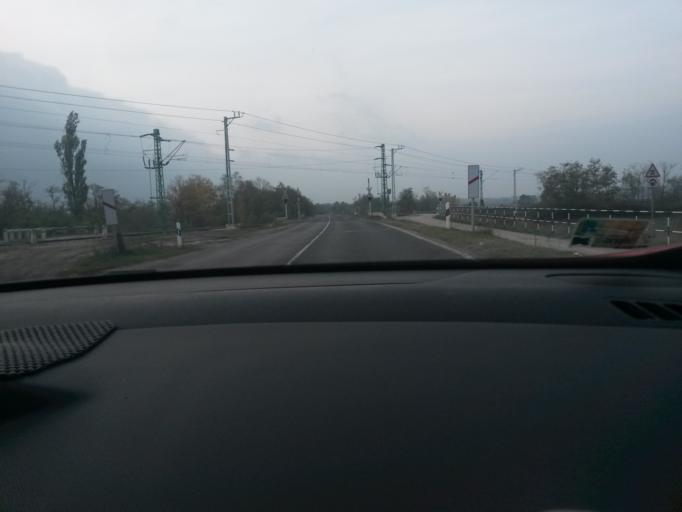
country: AT
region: Burgenland
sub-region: Politischer Bezirk Neusiedl am See
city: Nickelsdorf
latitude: 47.9231
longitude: 17.1301
